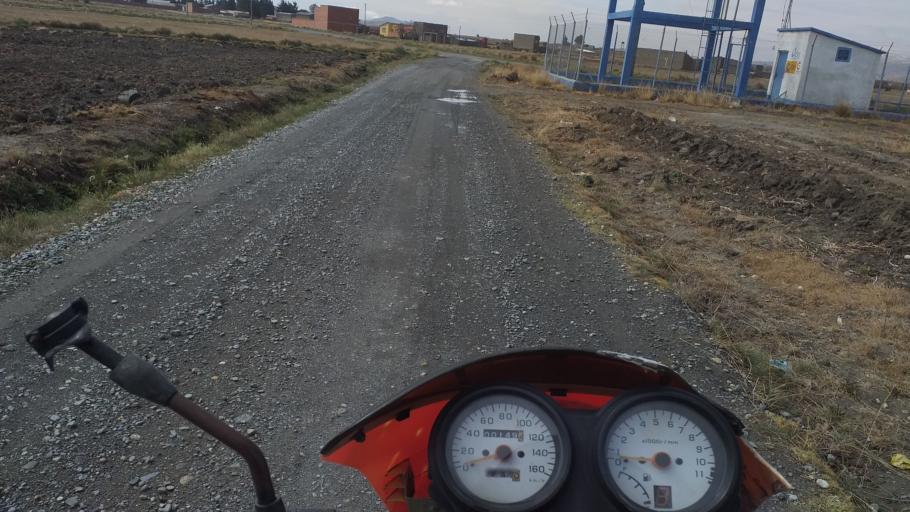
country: BO
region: La Paz
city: Achacachi
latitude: -16.0146
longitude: -68.7075
